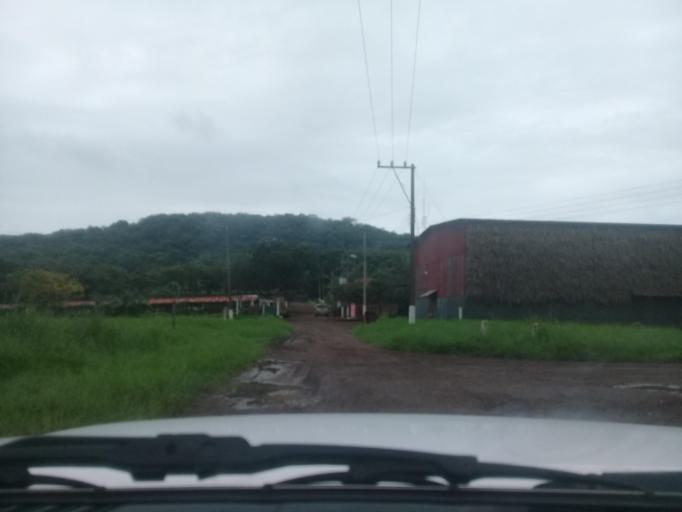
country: MX
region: Veracruz
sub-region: San Andres Tuxtla
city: Cerro las Iguanas
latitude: 18.4257
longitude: -95.1949
